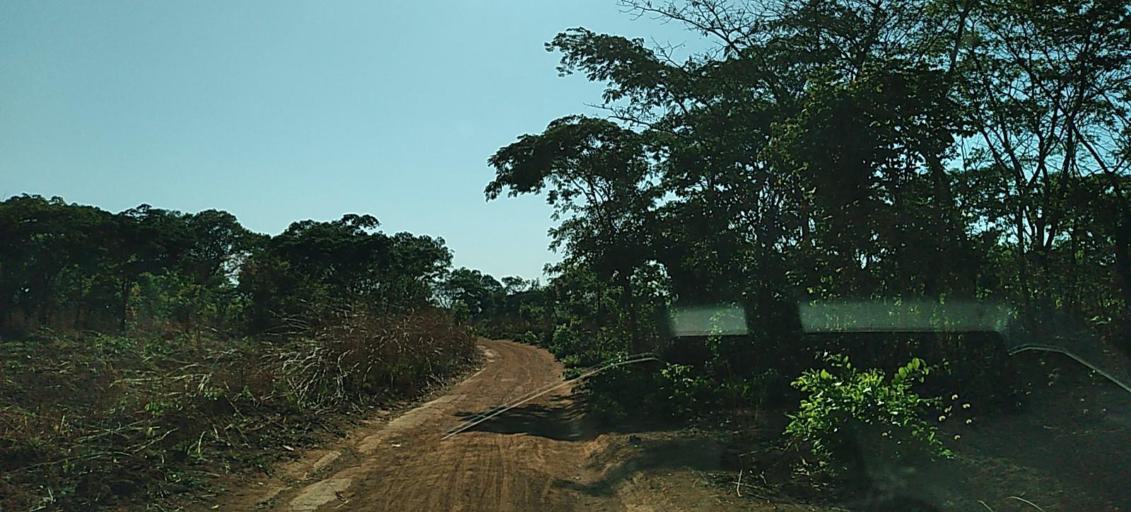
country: ZM
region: Copperbelt
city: Chililabombwe
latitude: -12.3691
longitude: 27.9175
